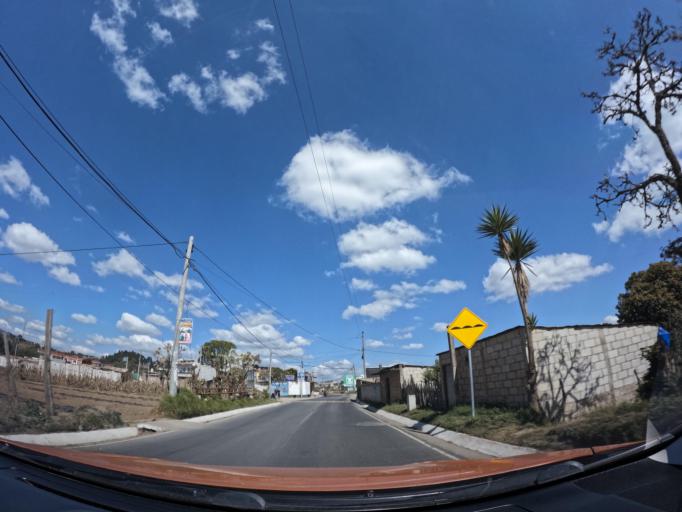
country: GT
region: Chimaltenango
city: Patzun
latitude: 14.6662
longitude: -91.0141
